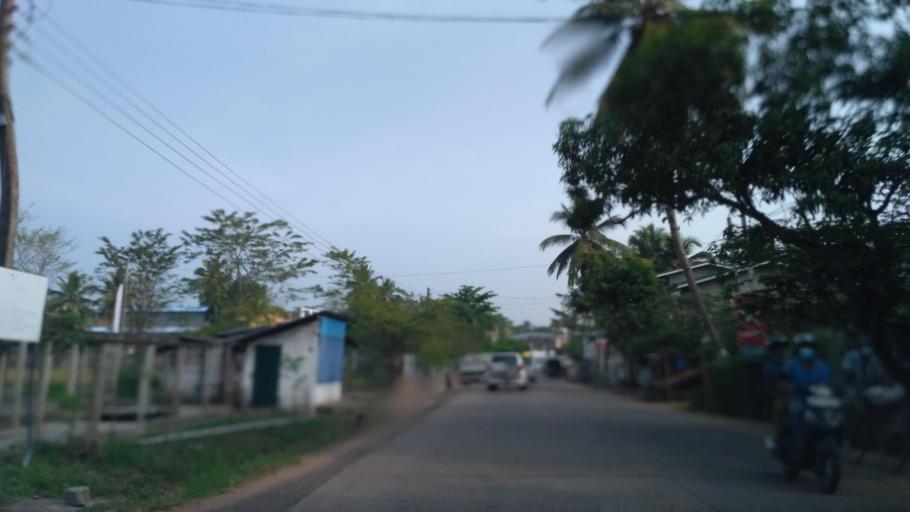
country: LK
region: North Western
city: Kuliyapitiya
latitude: 7.3266
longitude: 80.0237
